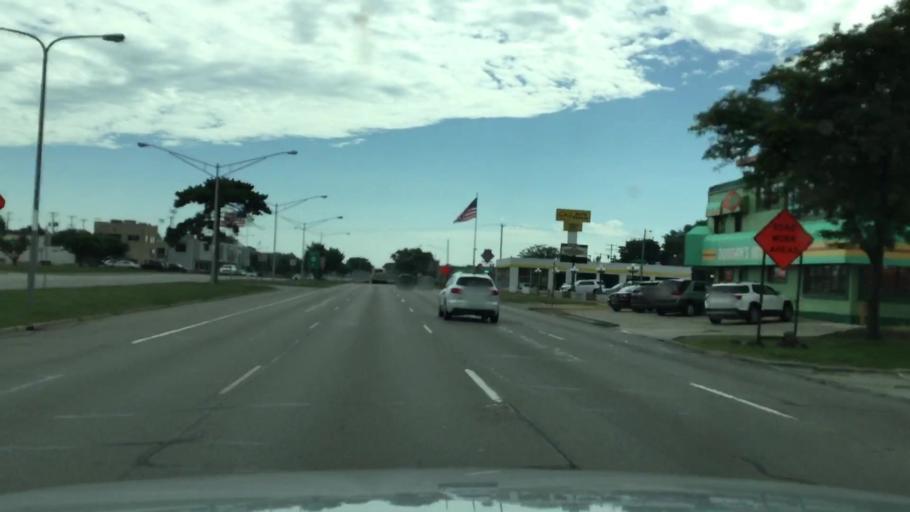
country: US
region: Michigan
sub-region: Oakland County
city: Berkley
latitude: 42.5221
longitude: -83.1905
